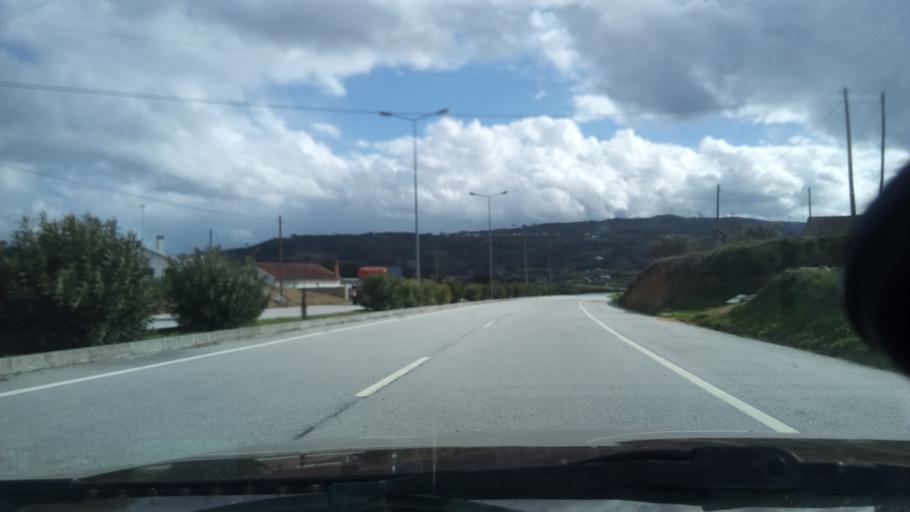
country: PT
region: Guarda
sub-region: Celorico da Beira
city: Celorico da Beira
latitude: 40.6404
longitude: -7.3902
